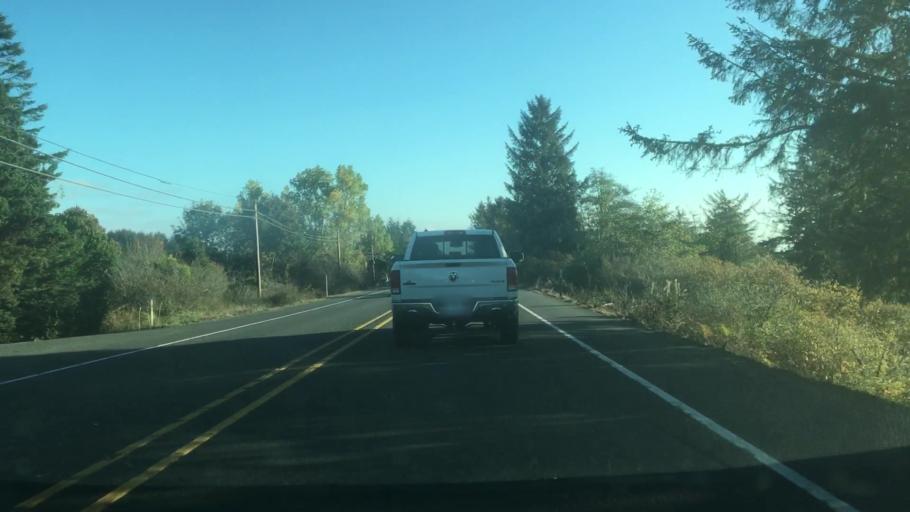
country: US
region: Oregon
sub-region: Clatsop County
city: Warrenton
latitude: 46.1061
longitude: -123.9210
